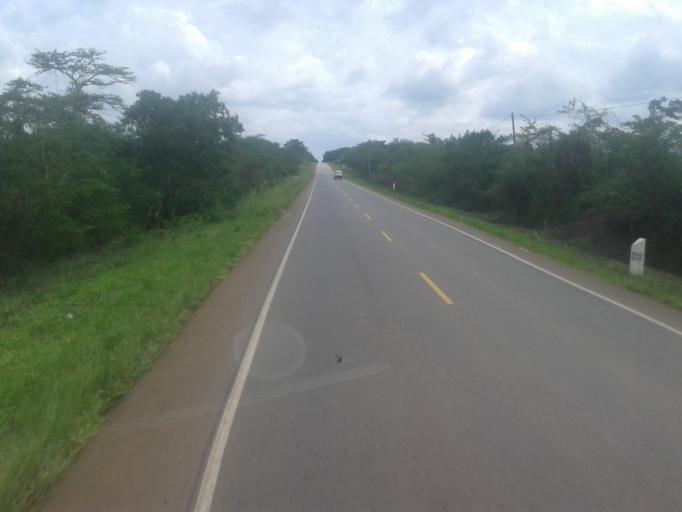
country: UG
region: Central Region
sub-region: Luwero District
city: Luwero
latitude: 1.0736
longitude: 32.4666
